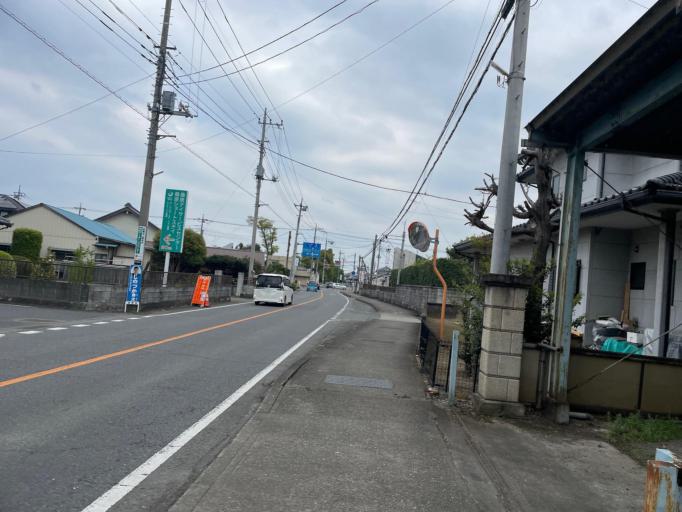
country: JP
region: Gunma
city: Isesaki
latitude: 36.2792
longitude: 139.2102
